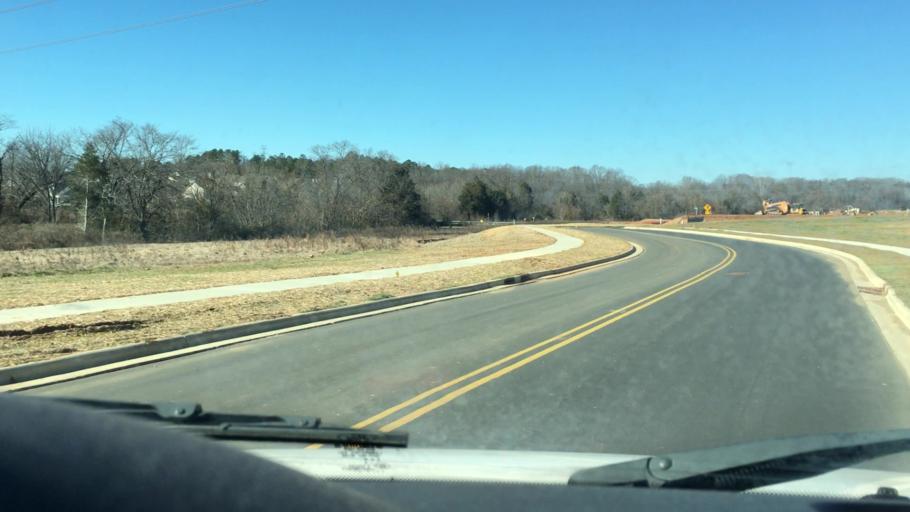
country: US
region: North Carolina
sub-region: Gaston County
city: Davidson
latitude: 35.4744
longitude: -80.8212
